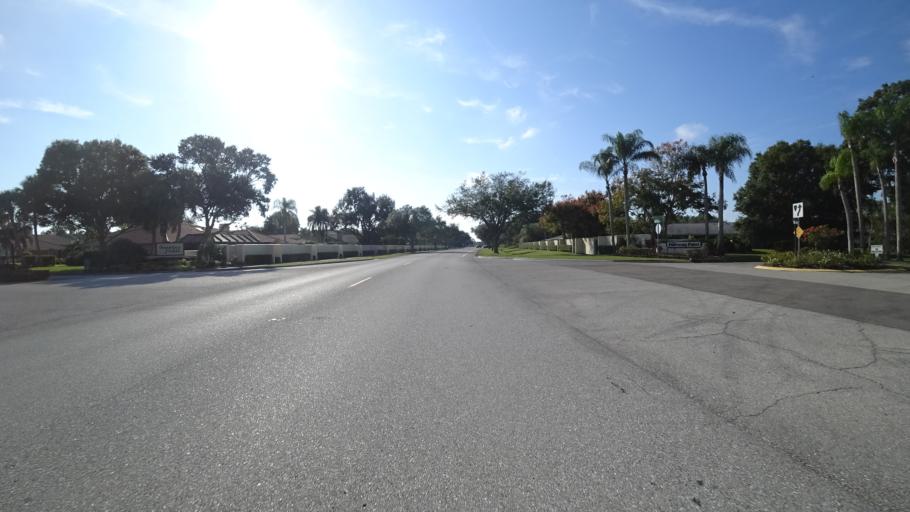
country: US
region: Florida
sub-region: Sarasota County
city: Desoto Lakes
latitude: 27.4171
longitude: -82.4921
